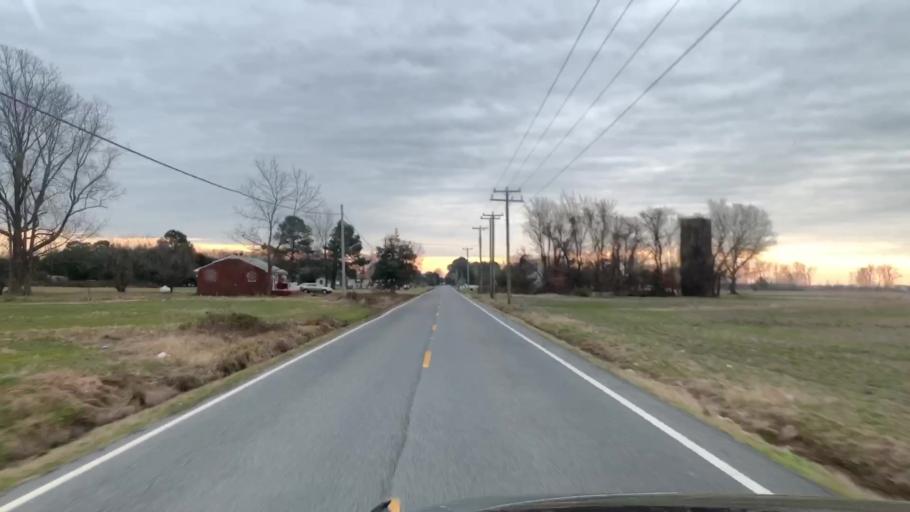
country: US
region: North Carolina
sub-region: Currituck County
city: Moyock
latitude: 36.6271
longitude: -76.1664
